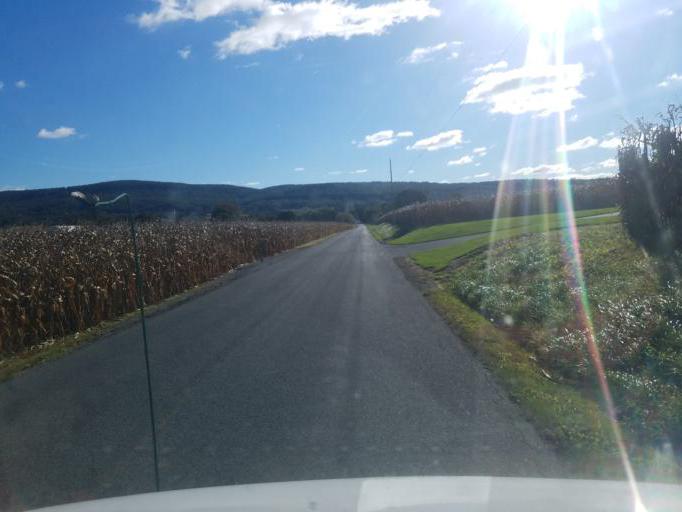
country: US
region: Pennsylvania
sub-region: Franklin County
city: Mont Alto
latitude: 39.8124
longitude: -77.5820
